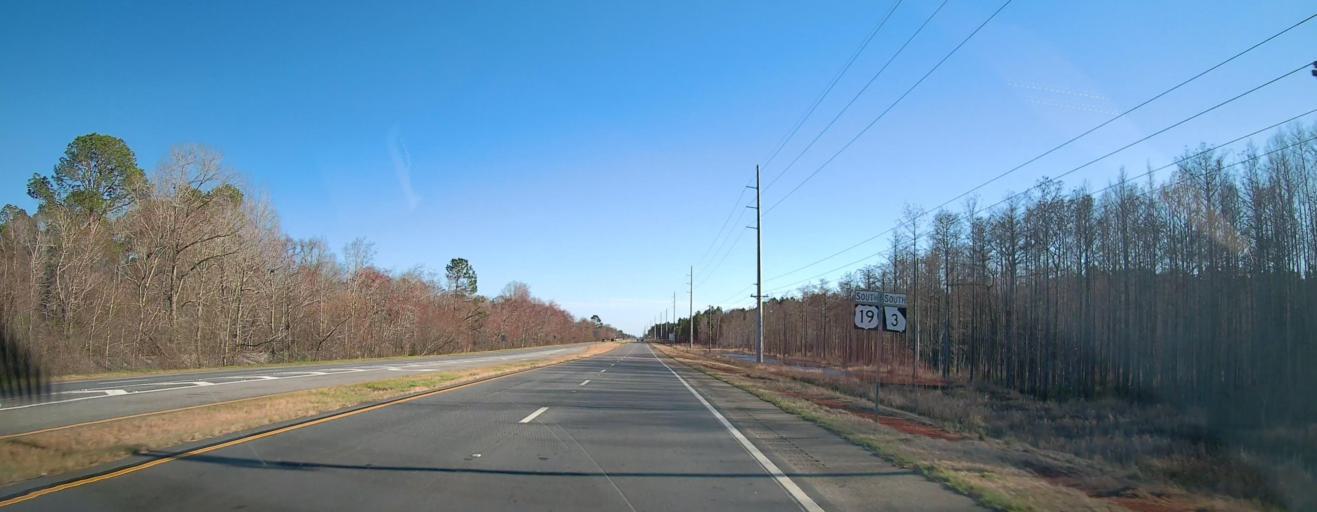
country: US
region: Georgia
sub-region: Lee County
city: Leesburg
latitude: 31.8828
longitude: -84.2438
